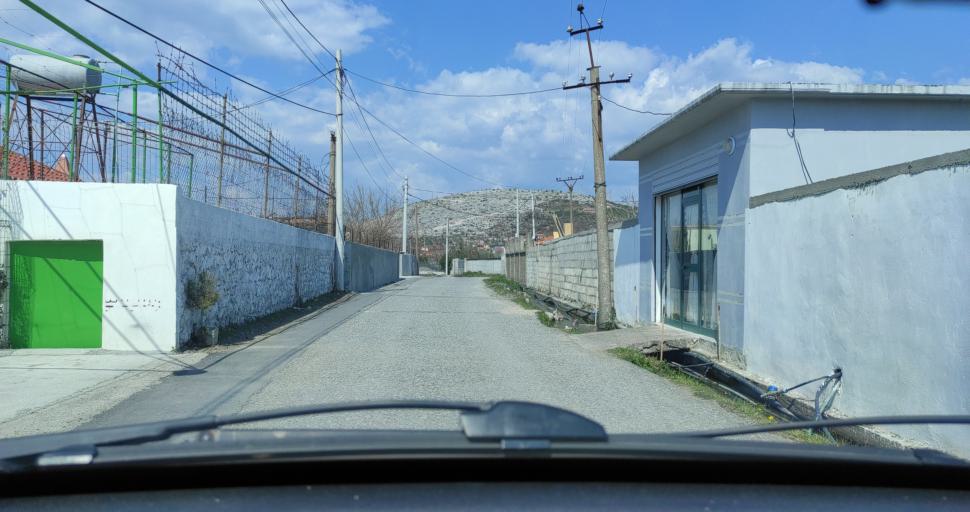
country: AL
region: Shkoder
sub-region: Rrethi i Shkodres
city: Vau i Dejes
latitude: 42.0053
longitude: 19.6420
